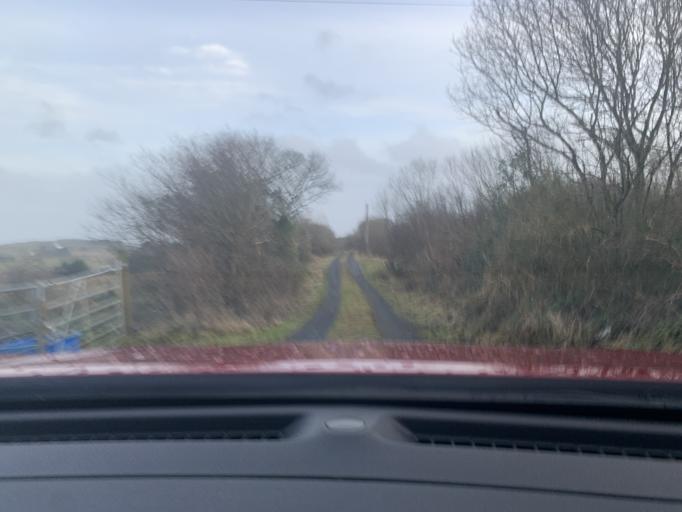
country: IE
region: Connaught
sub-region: Roscommon
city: Ballaghaderreen
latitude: 53.9529
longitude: -8.5378
